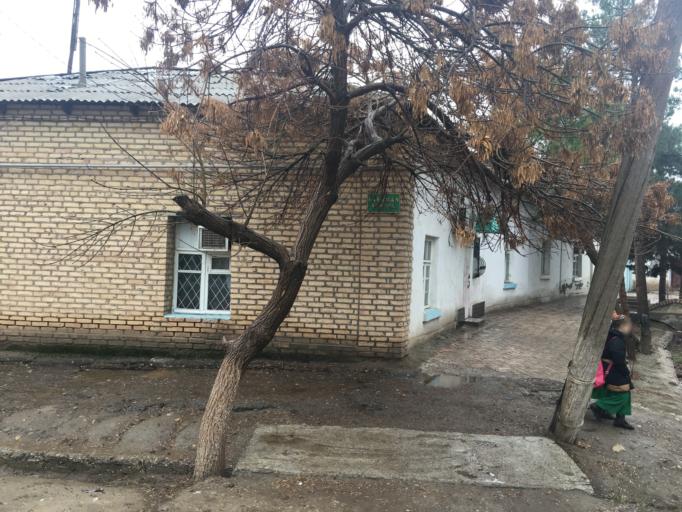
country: TM
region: Mary
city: Yoloeten
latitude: 37.2995
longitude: 62.3615
